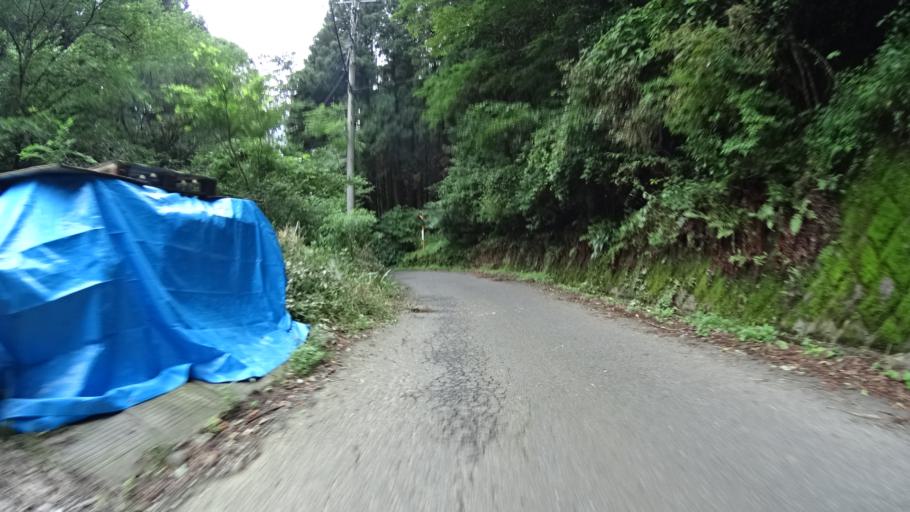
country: JP
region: Kanagawa
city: Atsugi
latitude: 35.4986
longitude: 139.2662
